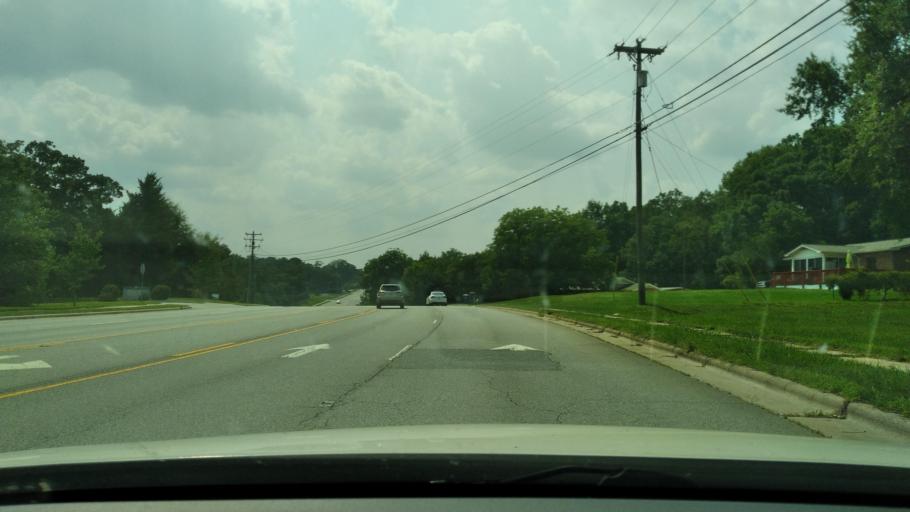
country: US
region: North Carolina
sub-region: Guilford County
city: Jamestown
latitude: 36.0391
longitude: -79.9106
